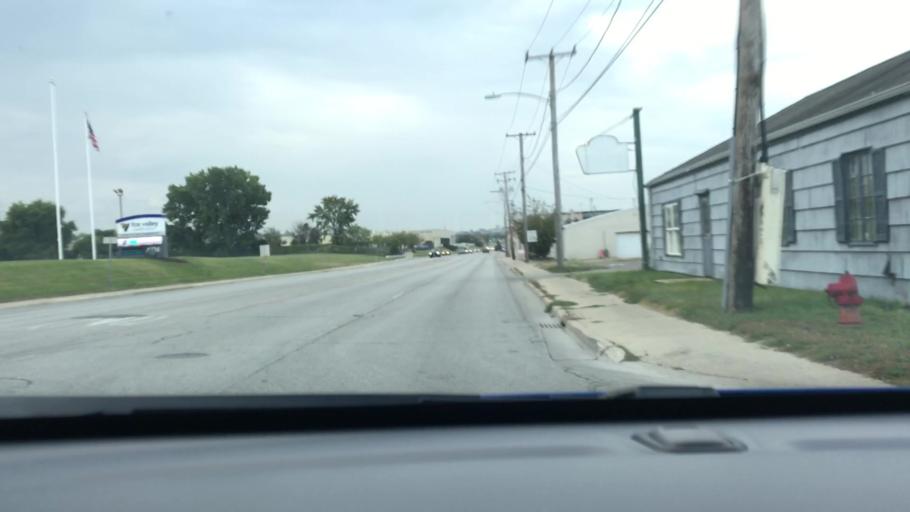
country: US
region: Illinois
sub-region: Kane County
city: Aurora
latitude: 41.7684
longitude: -88.3062
